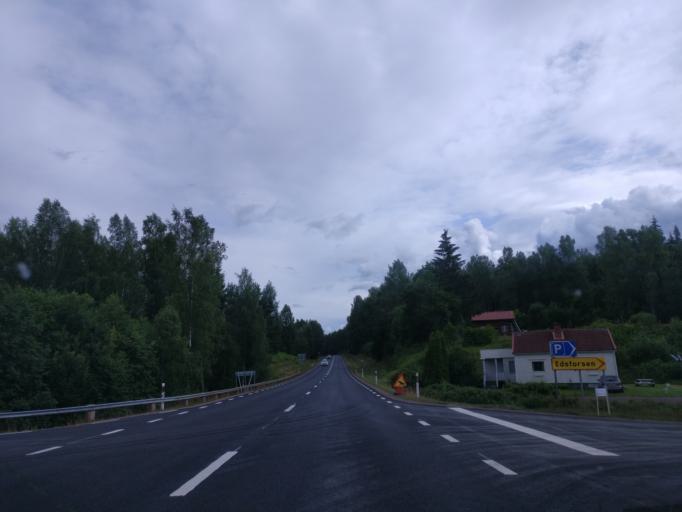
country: SE
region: Vaermland
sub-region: Hagfors Kommun
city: Ekshaerad
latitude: 60.0606
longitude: 13.5519
